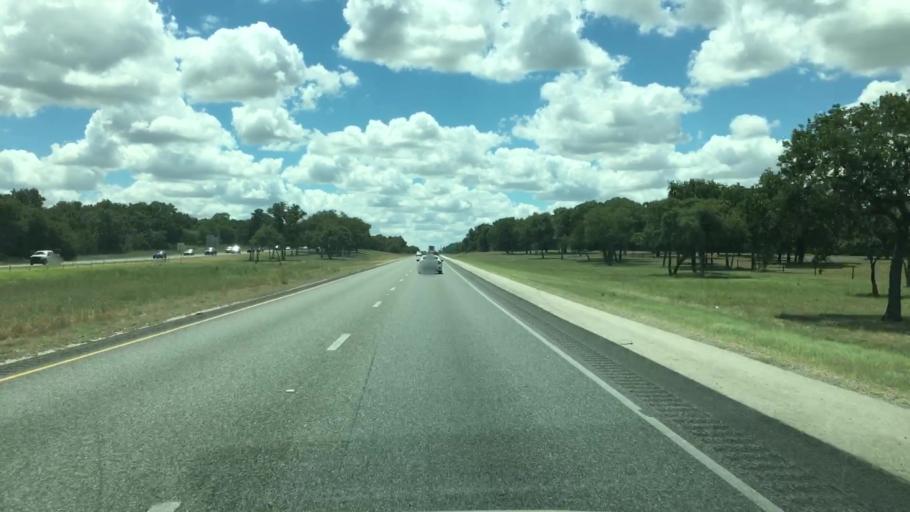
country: US
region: Texas
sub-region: Bexar County
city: Elmendorf
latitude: 29.2015
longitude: -98.4194
